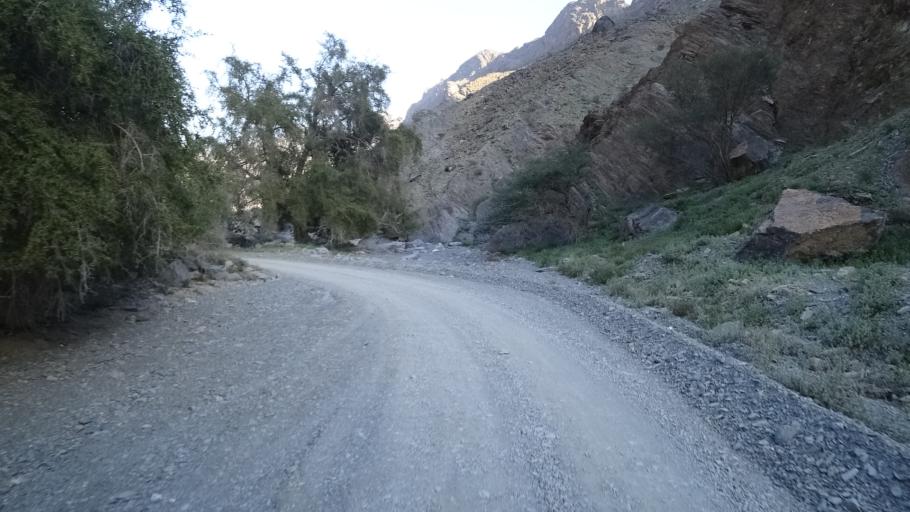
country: OM
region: Al Batinah
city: Bayt al `Awabi
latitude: 23.2545
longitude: 57.4048
